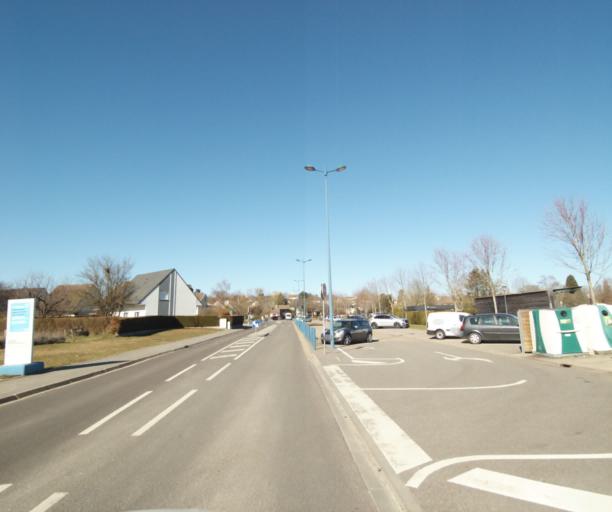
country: FR
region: Lorraine
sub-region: Departement de Meurthe-et-Moselle
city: Vandoeuvre-les-Nancy
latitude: 48.6486
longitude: 6.1949
